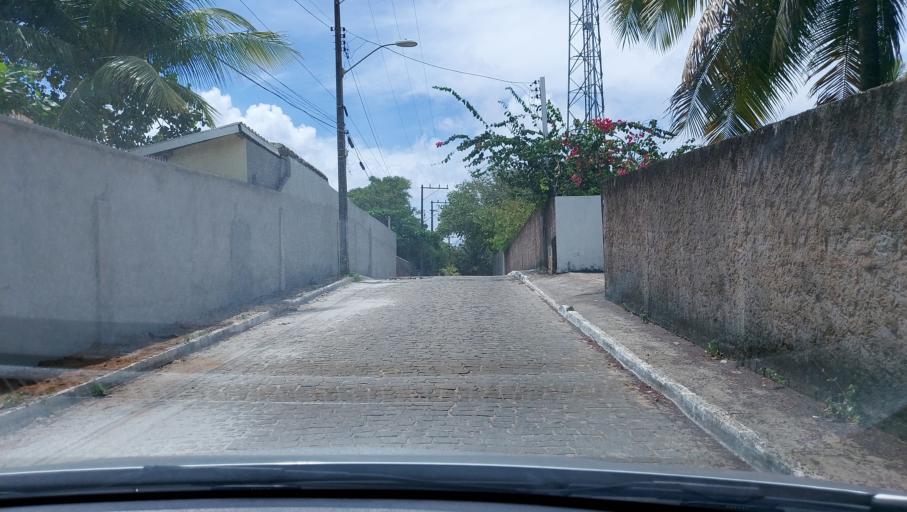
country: BR
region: Bahia
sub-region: Mata De Sao Joao
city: Mata de Sao Joao
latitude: -12.6269
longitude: -38.0474
